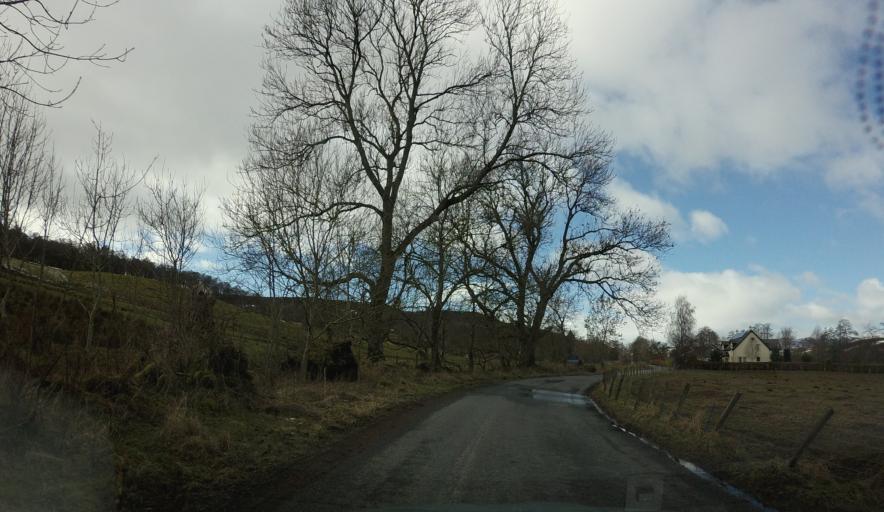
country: GB
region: Scotland
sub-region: Perth and Kinross
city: Pitlochry
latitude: 56.6456
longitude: -3.7143
